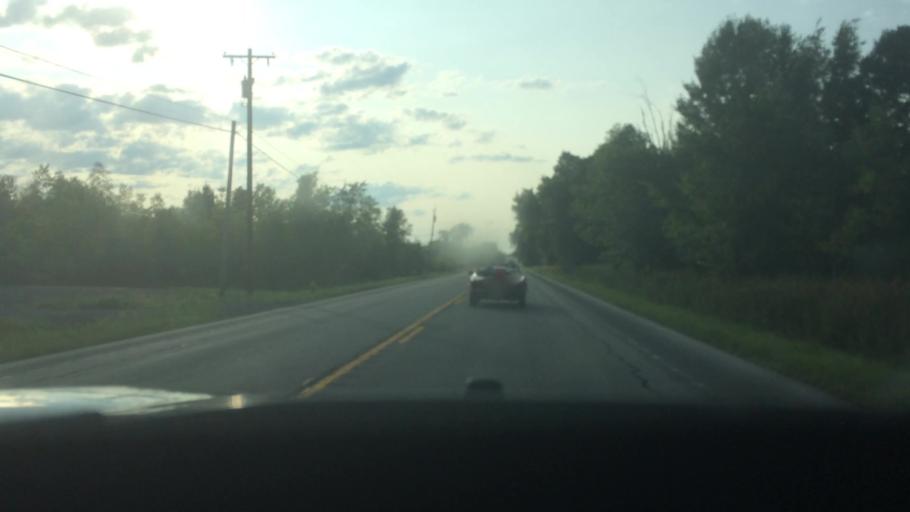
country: US
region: New York
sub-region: St. Lawrence County
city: Canton
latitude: 44.6508
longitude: -75.2990
